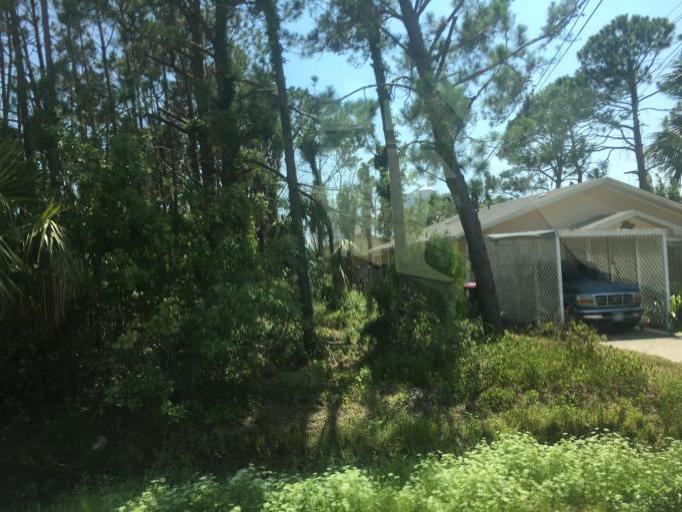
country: US
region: Florida
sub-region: Bay County
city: Lower Grand Lagoon
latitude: 30.1531
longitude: -85.7635
